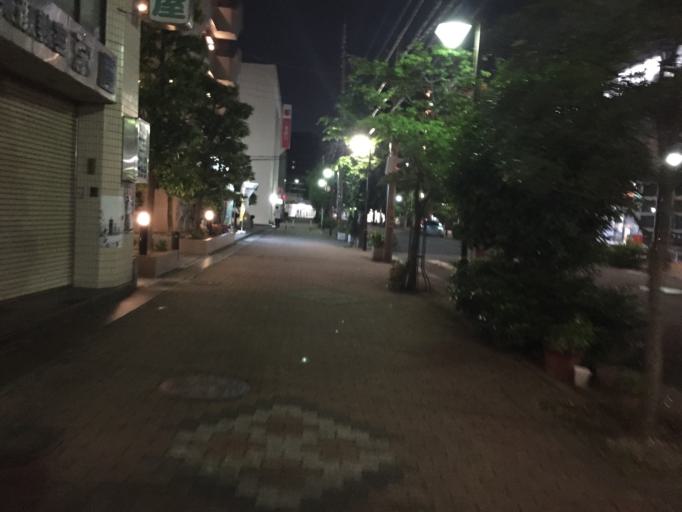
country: JP
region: Mie
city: Yokkaichi
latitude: 34.9661
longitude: 136.6278
